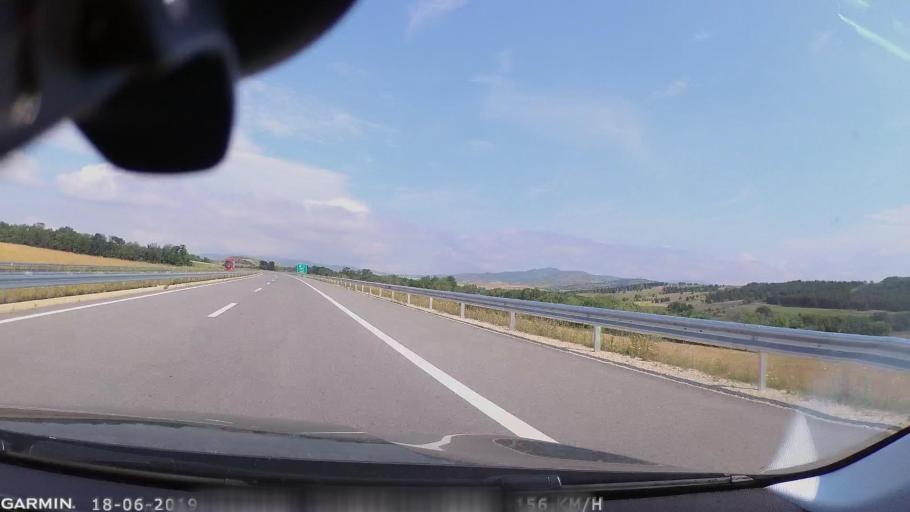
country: MK
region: Sveti Nikole
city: Gorobinci
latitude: 41.9086
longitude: 21.9043
